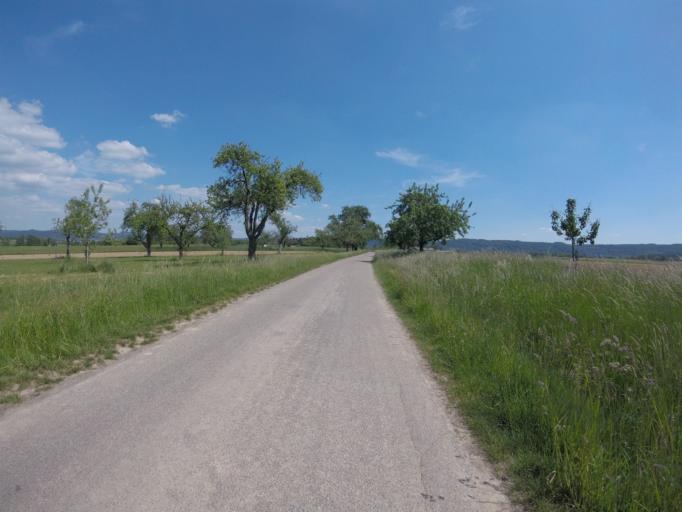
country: DE
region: Baden-Wuerttemberg
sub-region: Regierungsbezirk Stuttgart
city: Allmersbach im Tal
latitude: 48.9229
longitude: 9.4524
